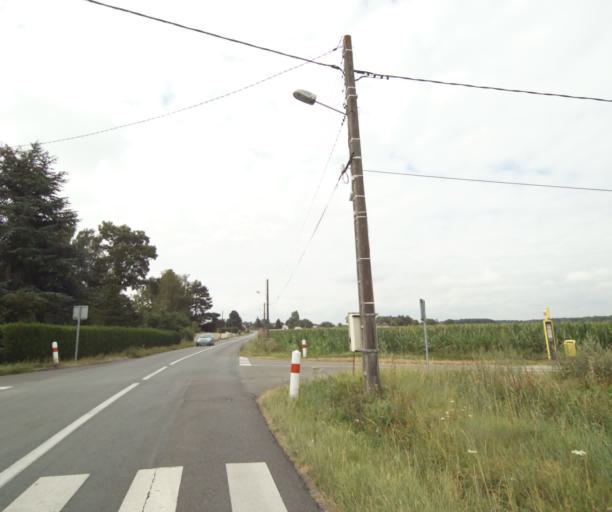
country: FR
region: Centre
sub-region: Departement du Loiret
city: Vennecy
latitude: 47.9258
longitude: 2.0462
